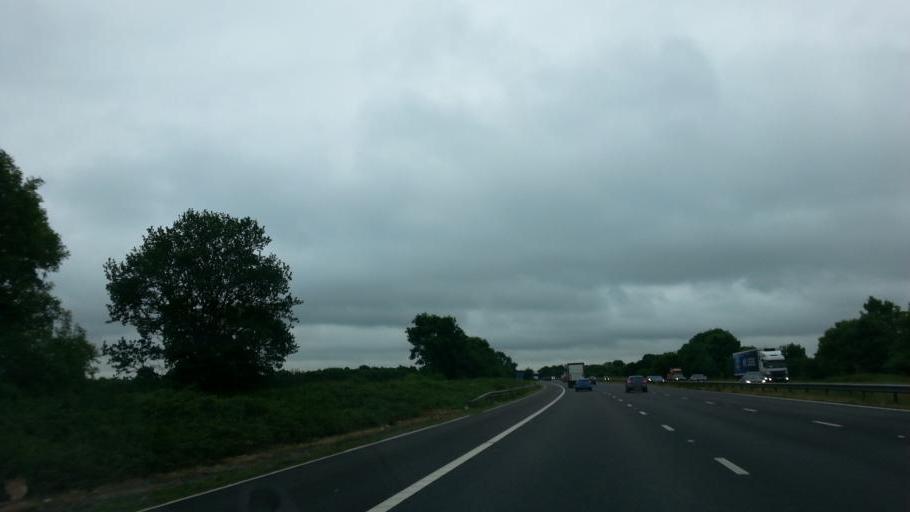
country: GB
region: England
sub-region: Leicestershire
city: Cosby
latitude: 52.5523
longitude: -1.1854
